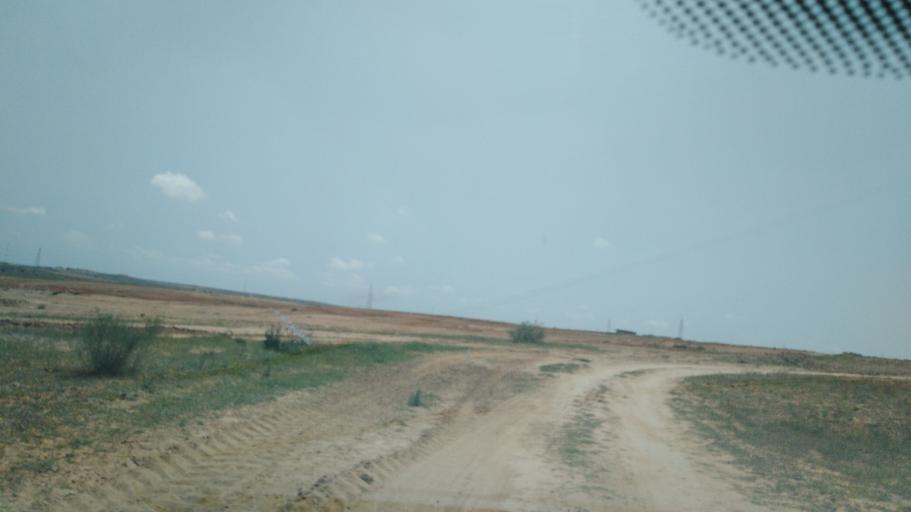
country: TN
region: Safaqis
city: Sfax
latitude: 34.7715
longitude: 10.5783
